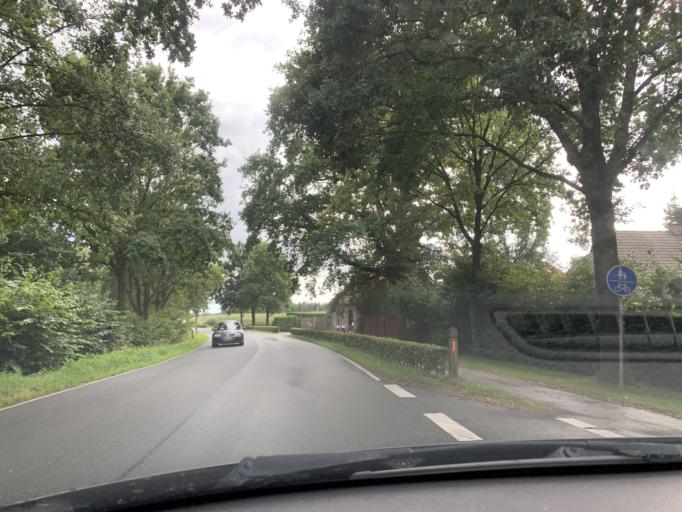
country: DE
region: Lower Saxony
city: Westerstede
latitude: 53.3116
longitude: 7.9170
